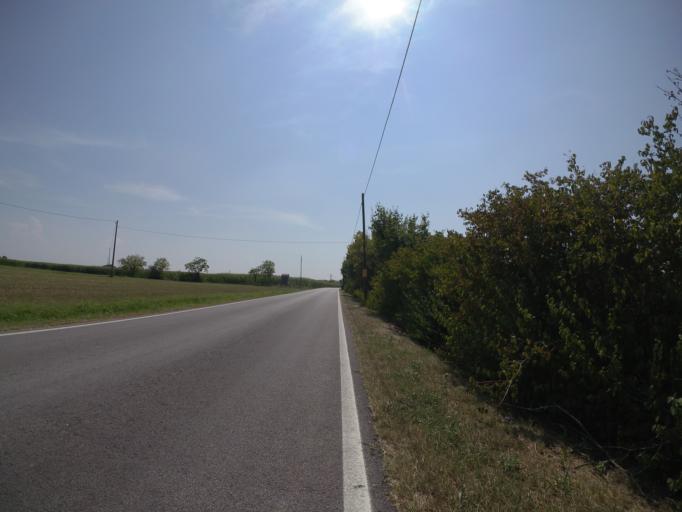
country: IT
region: Friuli Venezia Giulia
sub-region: Provincia di Udine
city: Pocenia
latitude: 45.8593
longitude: 13.0890
